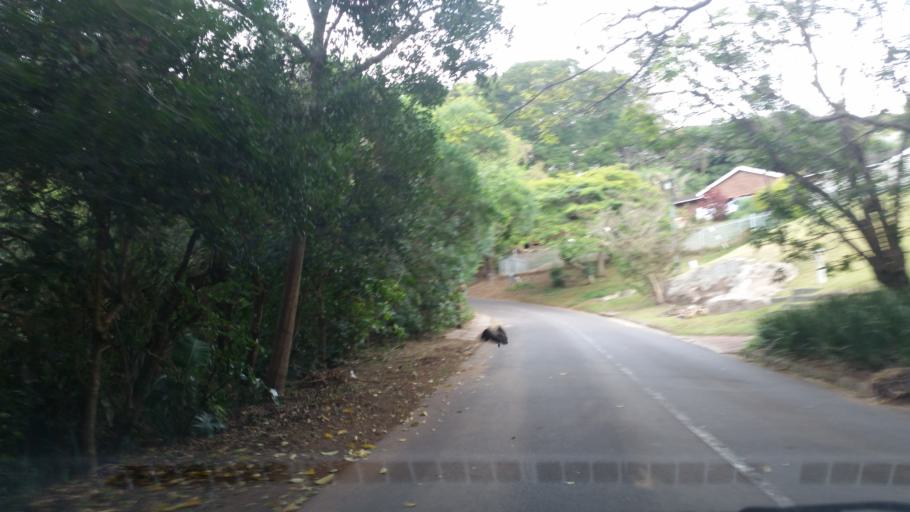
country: ZA
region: KwaZulu-Natal
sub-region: eThekwini Metropolitan Municipality
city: Berea
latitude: -29.8256
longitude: 30.9300
